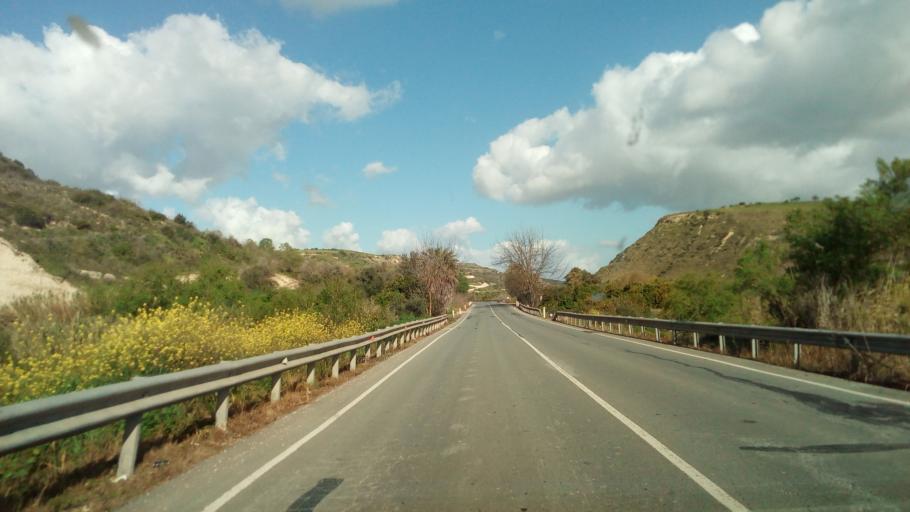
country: CY
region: Pafos
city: Polis
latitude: 34.9578
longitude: 32.4628
